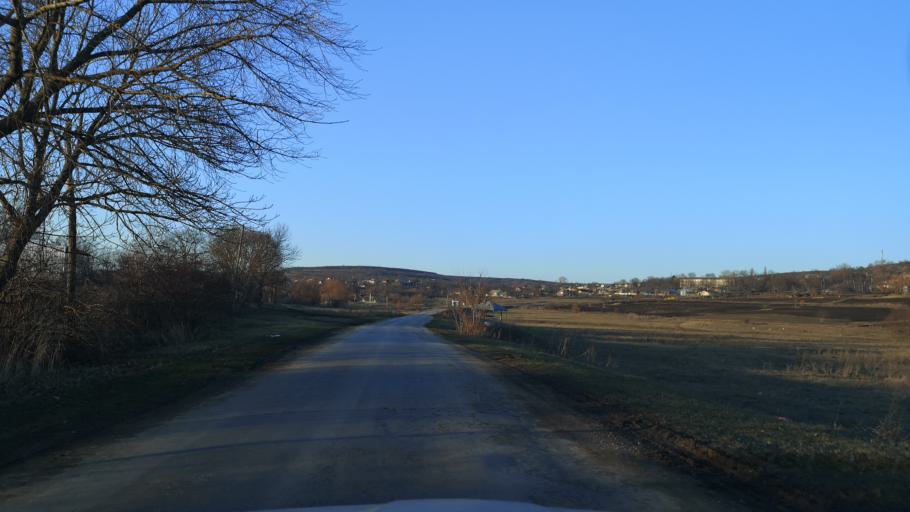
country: MD
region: Orhei
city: Orhei
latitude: 47.3494
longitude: 28.6963
